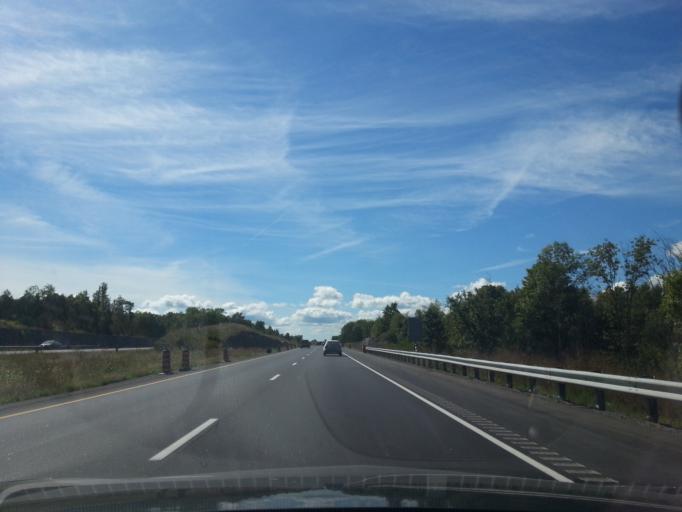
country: CA
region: Ontario
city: Skatepark
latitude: 44.2774
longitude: -76.8365
